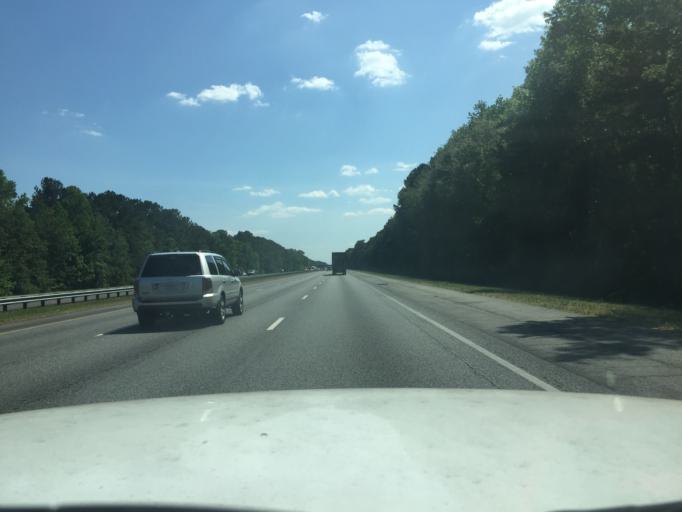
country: US
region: Georgia
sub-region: Chatham County
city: Pooler
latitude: 32.0521
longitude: -81.2573
